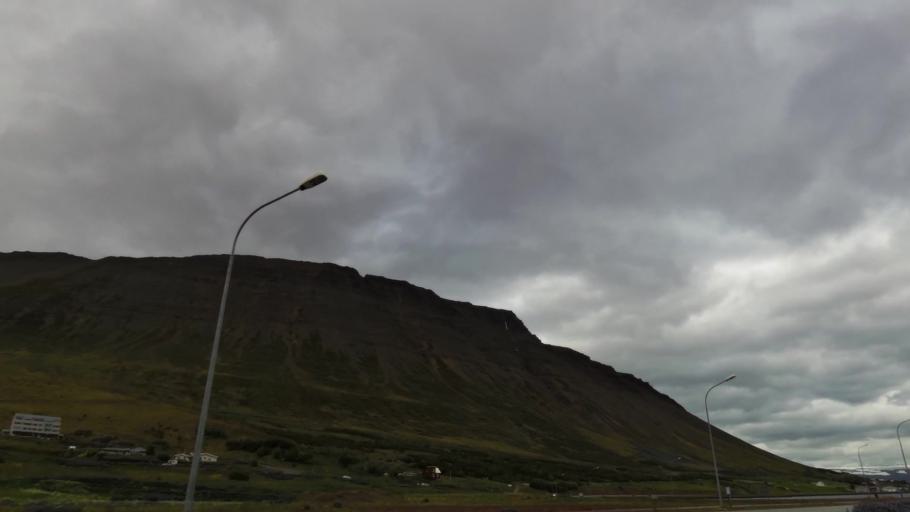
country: IS
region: Westfjords
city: Isafjoerdur
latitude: 66.0607
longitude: -23.1763
